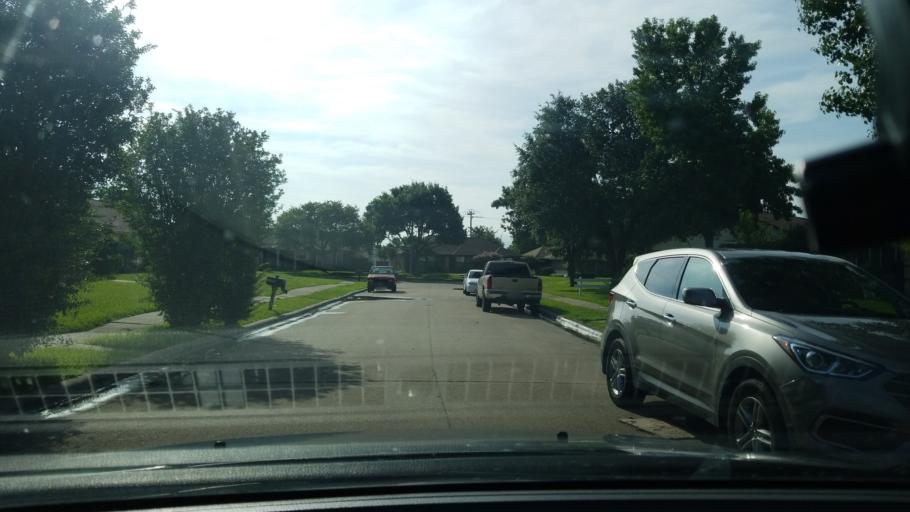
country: US
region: Texas
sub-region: Dallas County
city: Mesquite
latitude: 32.8020
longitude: -96.6127
